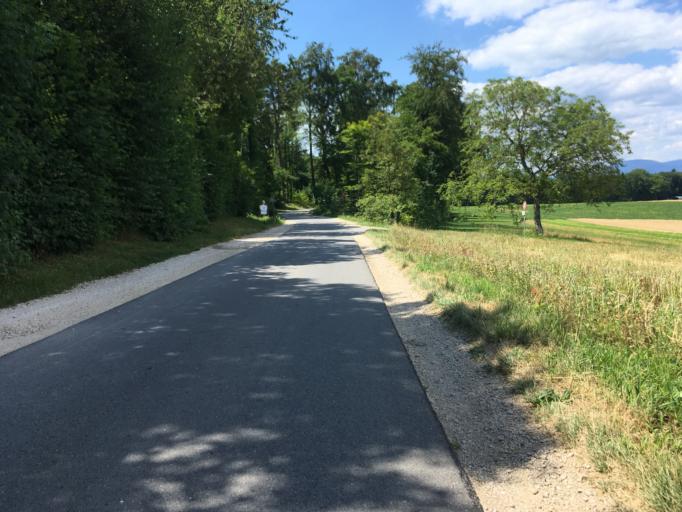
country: CH
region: Fribourg
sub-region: Broye District
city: Domdidier
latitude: 46.9223
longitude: 6.9741
